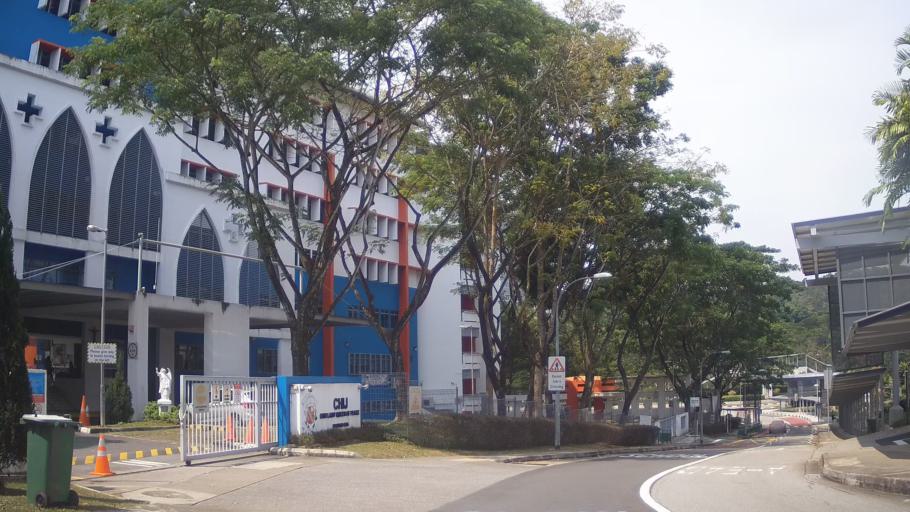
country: MY
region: Johor
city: Johor Bahru
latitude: 1.3673
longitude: 103.7679
